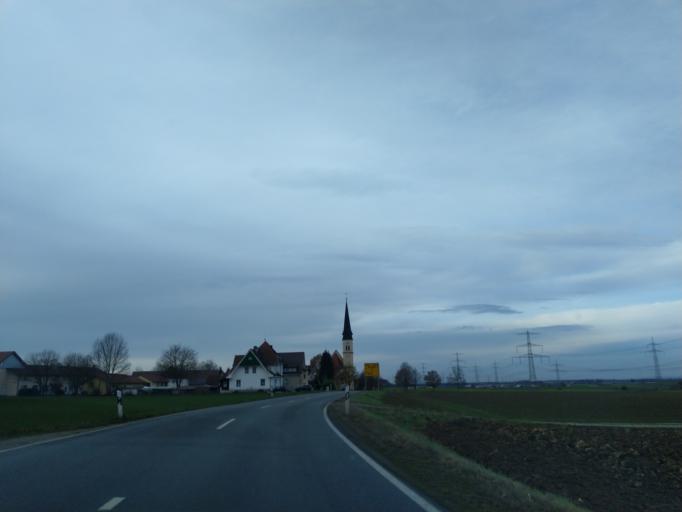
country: DE
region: Bavaria
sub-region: Lower Bavaria
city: Kunzing
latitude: 48.6524
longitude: 13.0512
